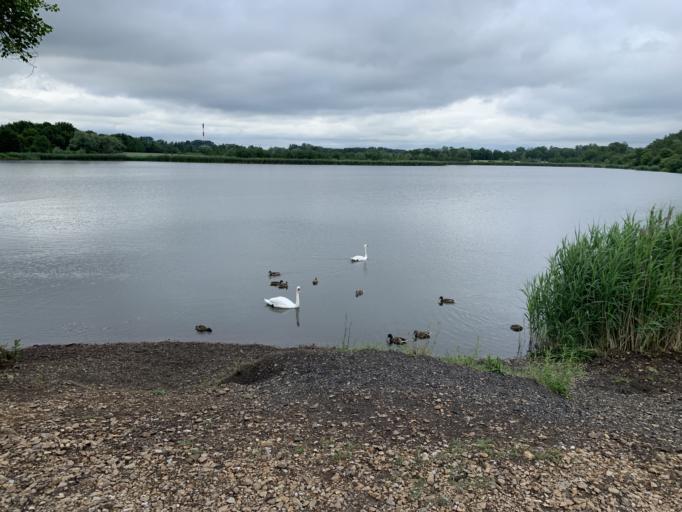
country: PL
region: Silesian Voivodeship
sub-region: Bytom
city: Bytom
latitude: 50.3292
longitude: 18.9556
